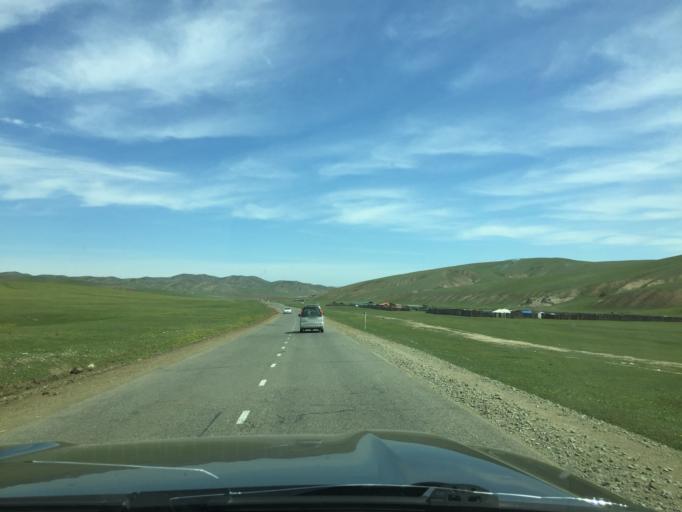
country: MN
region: Central Aimak
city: Bornuur
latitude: 48.6695
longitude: 106.1357
